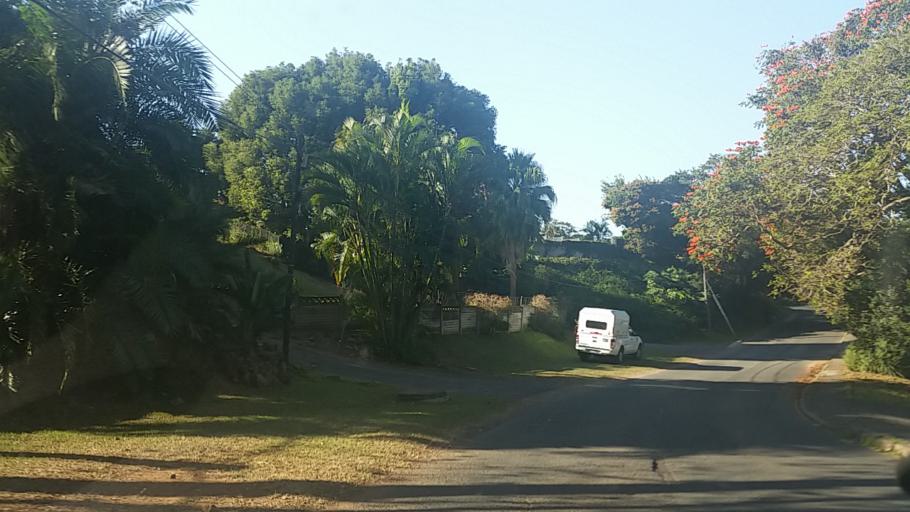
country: ZA
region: KwaZulu-Natal
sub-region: eThekwini Metropolitan Municipality
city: Berea
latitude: -29.8438
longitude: 30.9137
